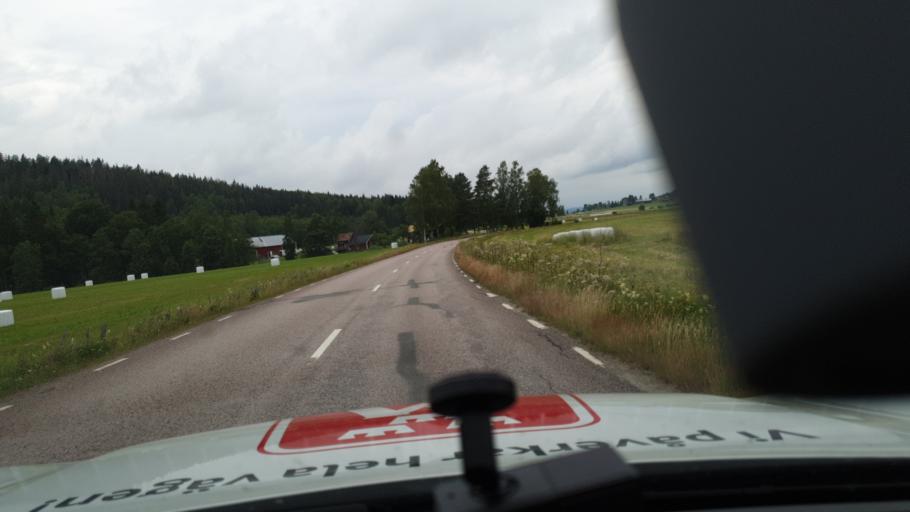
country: SE
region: Vaermland
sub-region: Sunne Kommun
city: Sunne
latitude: 59.8125
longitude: 13.2241
